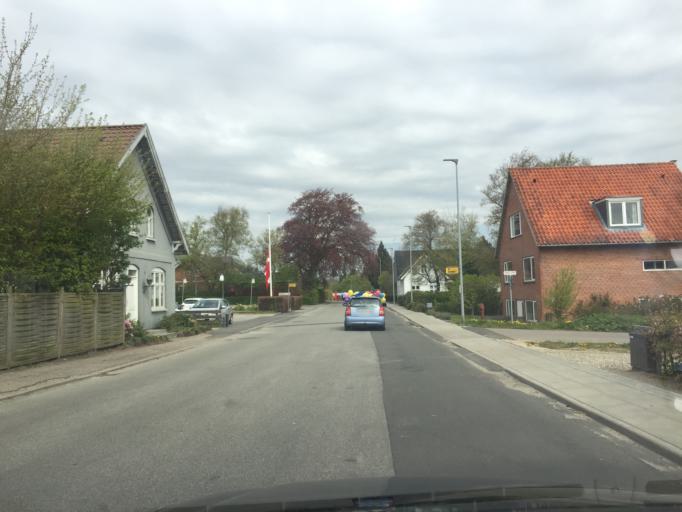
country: DK
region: South Denmark
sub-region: Kolding Kommune
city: Sonder Bjert
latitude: 55.4563
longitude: 9.5574
